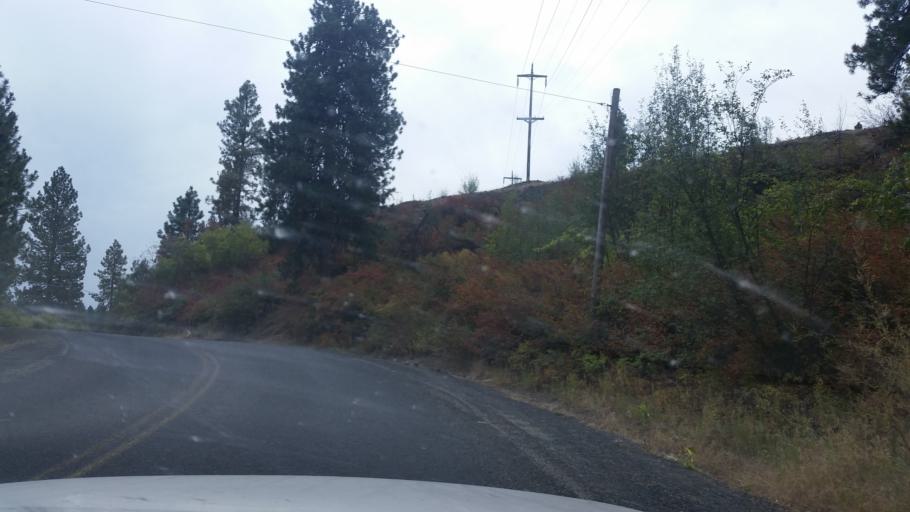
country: US
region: Washington
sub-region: Spokane County
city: Spokane
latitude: 47.6553
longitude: -117.4969
